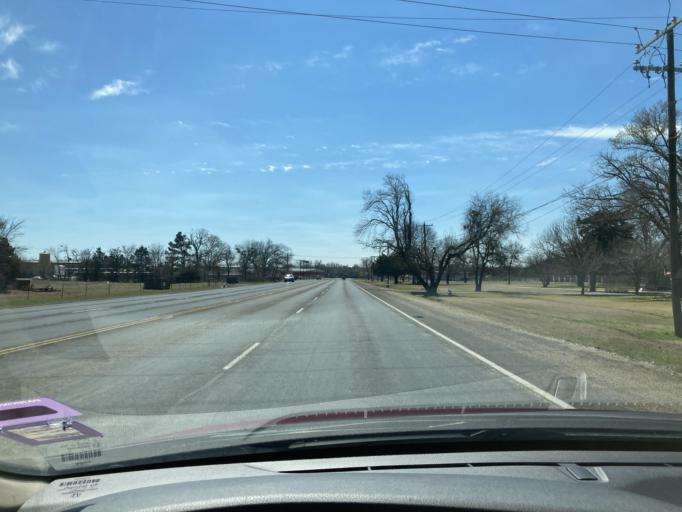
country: US
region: Texas
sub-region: Navarro County
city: Corsicana
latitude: 32.1111
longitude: -96.4641
